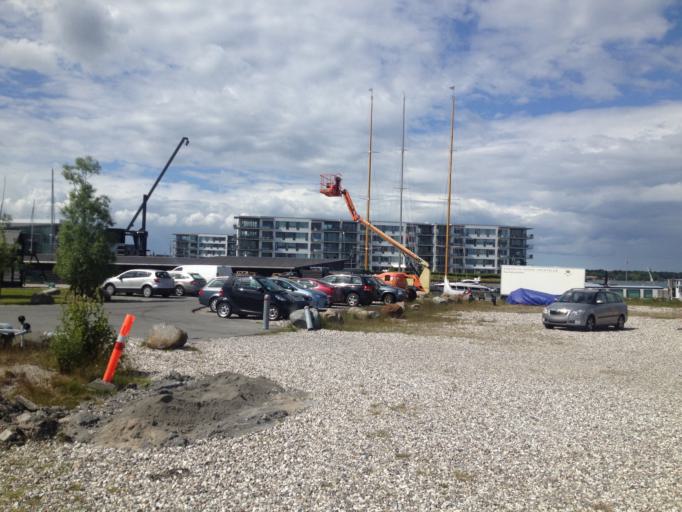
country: DK
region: Capital Region
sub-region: Gentofte Kommune
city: Charlottenlund
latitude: 55.7254
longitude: 12.5882
